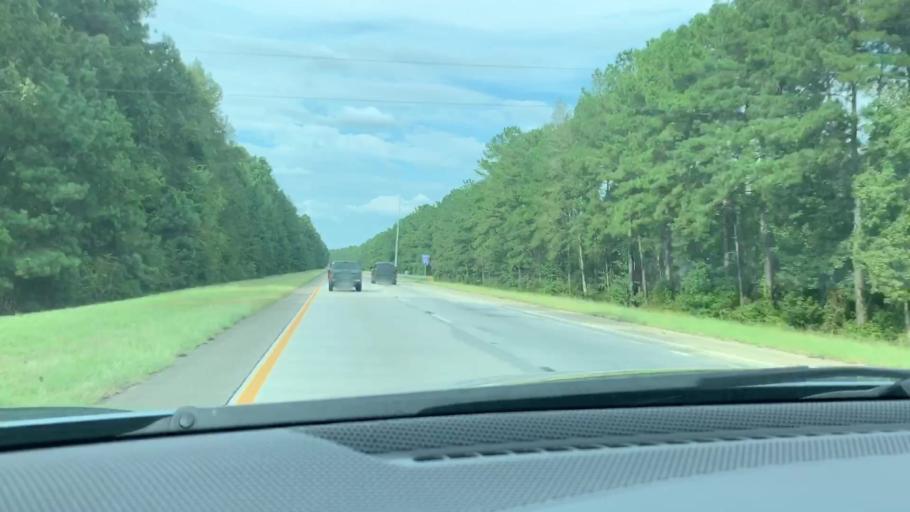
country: US
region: South Carolina
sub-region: Colleton County
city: Walterboro
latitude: 33.0105
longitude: -80.6671
